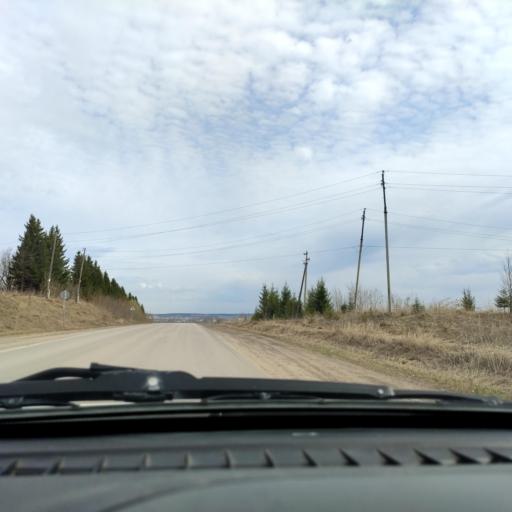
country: RU
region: Perm
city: Lobanovo
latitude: 57.8582
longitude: 56.2960
